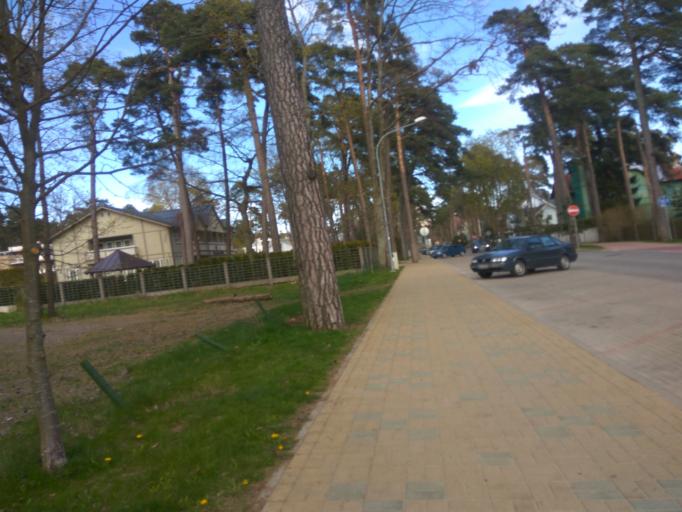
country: LV
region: Jurmala
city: Jurmala
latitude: 56.9765
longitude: 23.8067
